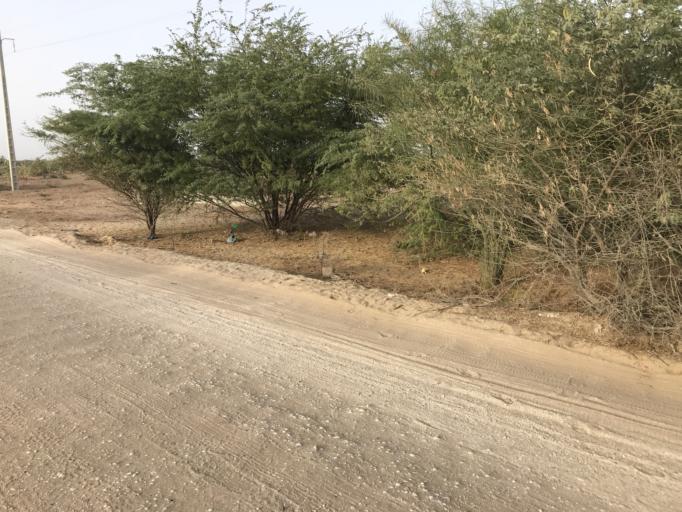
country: SN
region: Saint-Louis
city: Saint-Louis
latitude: 16.0294
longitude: -16.4451
